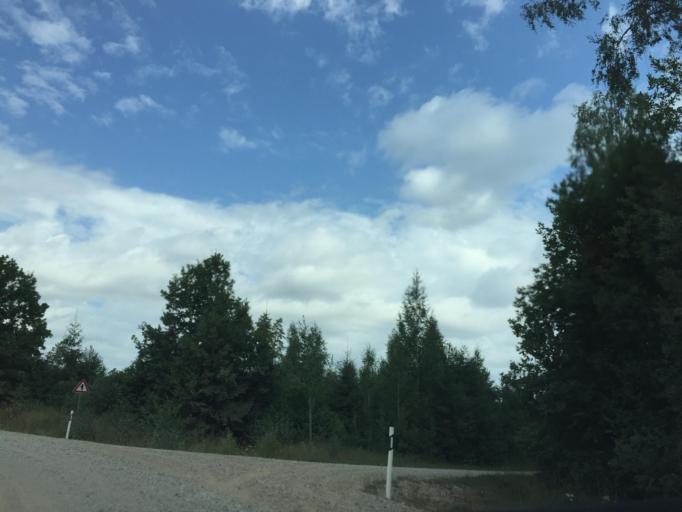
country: LV
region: Kandava
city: Kandava
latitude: 57.0118
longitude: 22.8361
